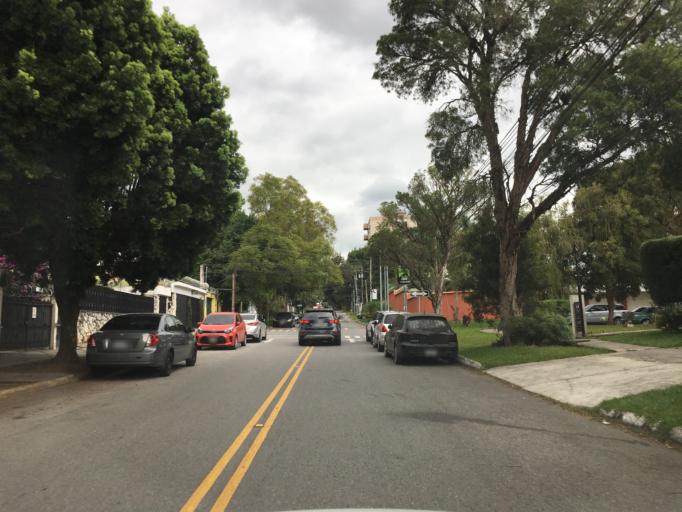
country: GT
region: Guatemala
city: Santa Catarina Pinula
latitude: 14.5916
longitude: -90.4939
